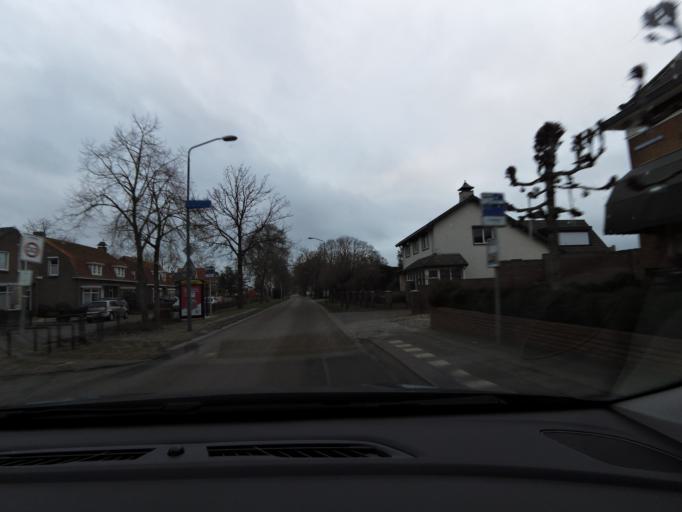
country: NL
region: North Brabant
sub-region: Gemeente Waalwijk
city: Waspik
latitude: 51.6798
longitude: 4.9840
